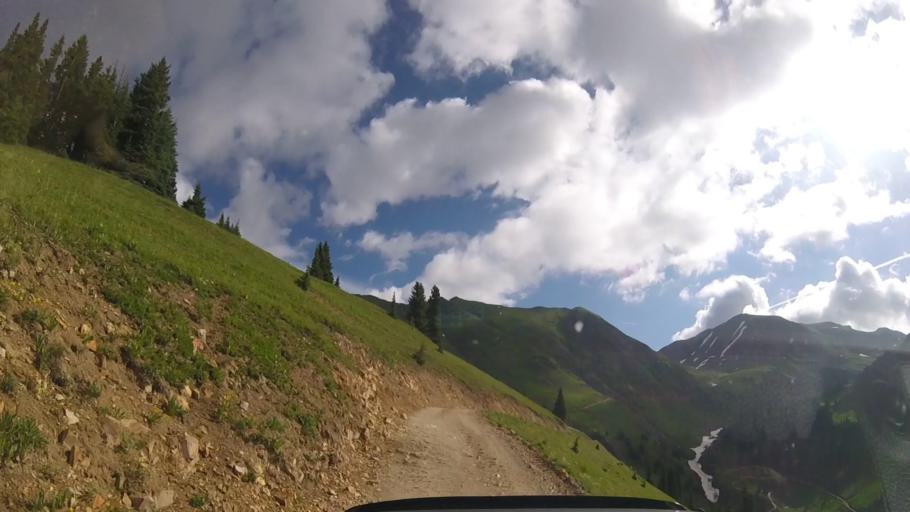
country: US
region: Colorado
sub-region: San Juan County
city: Silverton
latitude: 37.9075
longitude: -107.6479
